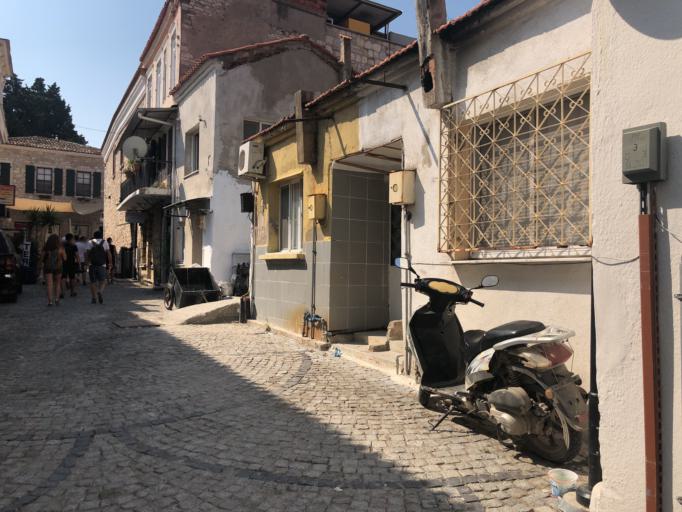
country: TR
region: Izmir
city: Urla
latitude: 38.3225
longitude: 26.7649
